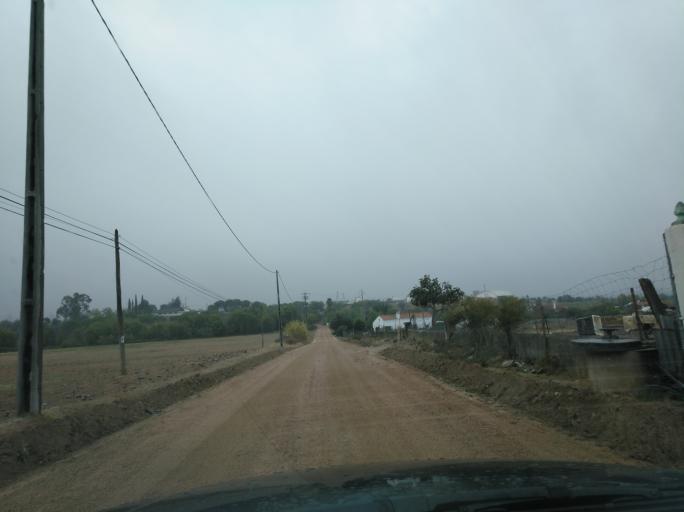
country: PT
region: Portalegre
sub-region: Campo Maior
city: Campo Maior
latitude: 38.9540
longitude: -7.0712
